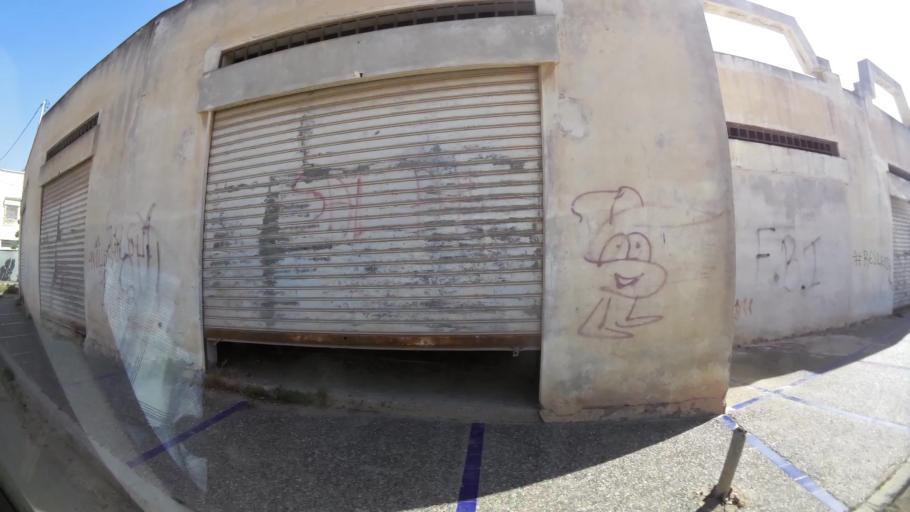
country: MA
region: Souss-Massa-Draa
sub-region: Inezgane-Ait Mellou
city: Inezgane
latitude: 30.3632
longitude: -9.5396
